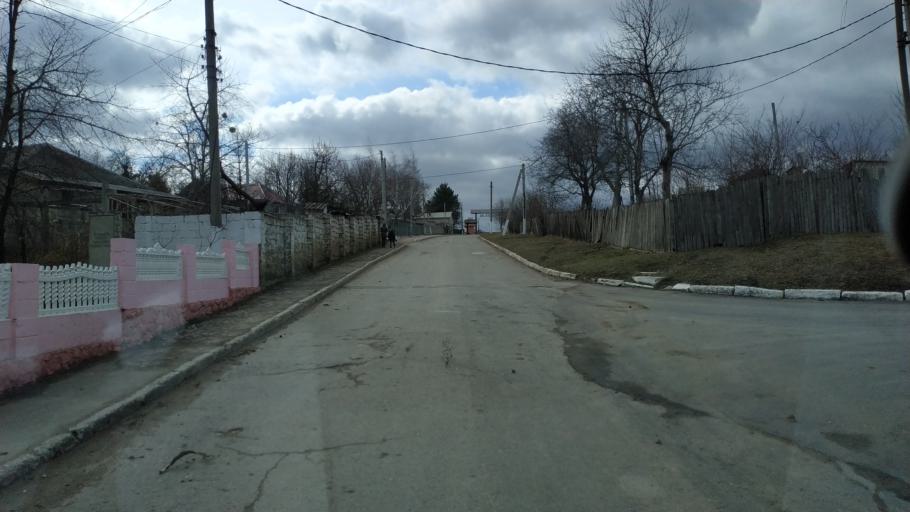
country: MD
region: Stinga Nistrului
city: Bucovat
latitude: 47.2284
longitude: 28.4414
